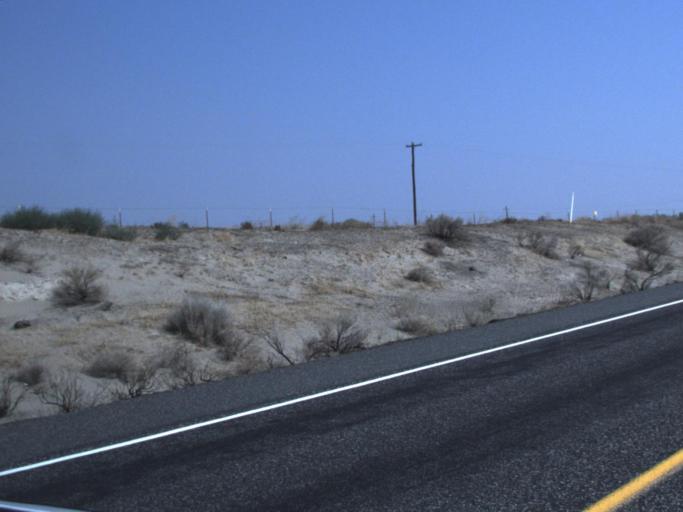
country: US
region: Washington
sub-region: Grant County
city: Desert Aire
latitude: 46.5770
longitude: -119.7329
